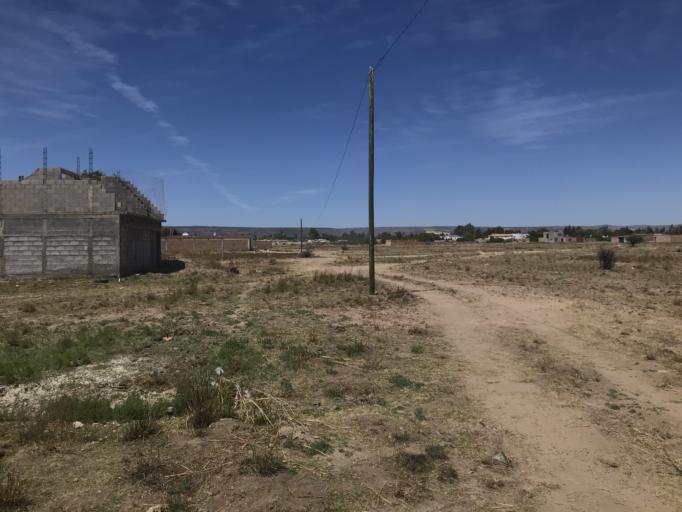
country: MX
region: Durango
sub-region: Durango
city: Sebastian Lerdo de Tejada
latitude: 23.9798
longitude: -104.6543
